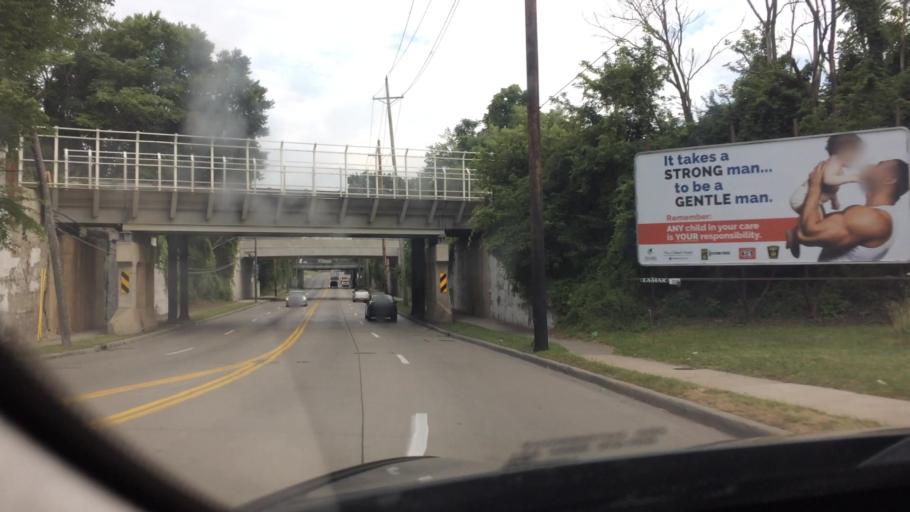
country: US
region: Ohio
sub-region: Wood County
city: Rossford
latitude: 41.6384
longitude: -83.5912
